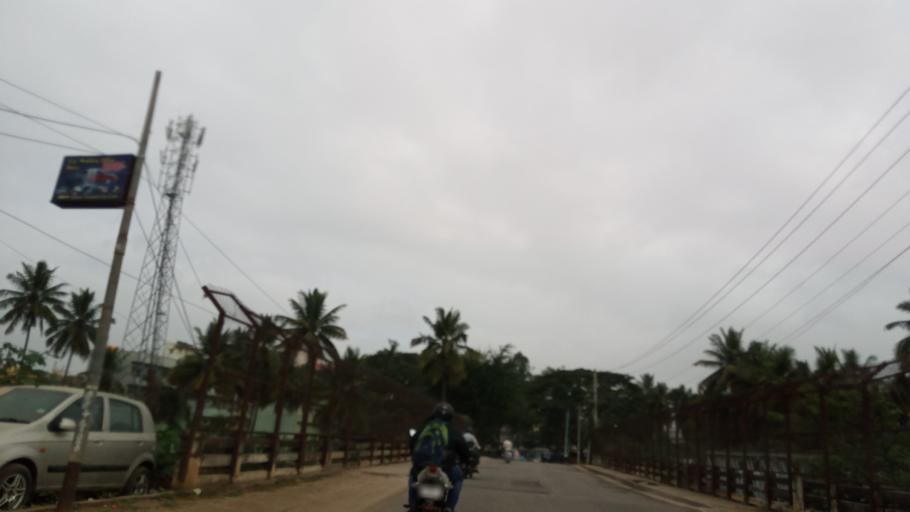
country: IN
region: Karnataka
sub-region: Bangalore Urban
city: Bangalore
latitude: 12.9087
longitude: 77.4872
